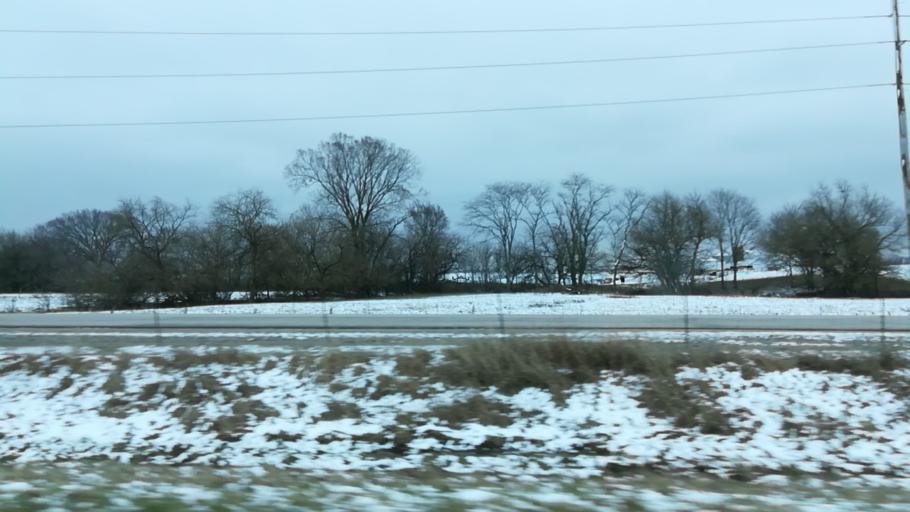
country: US
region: Illinois
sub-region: Madison County
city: Highland
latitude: 38.8044
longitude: -89.5935
